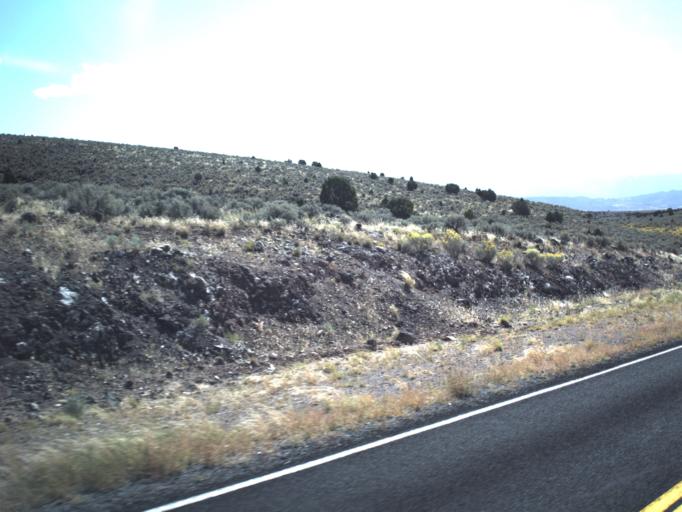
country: US
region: Utah
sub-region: Iron County
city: Parowan
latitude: 38.0341
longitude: -112.9984
